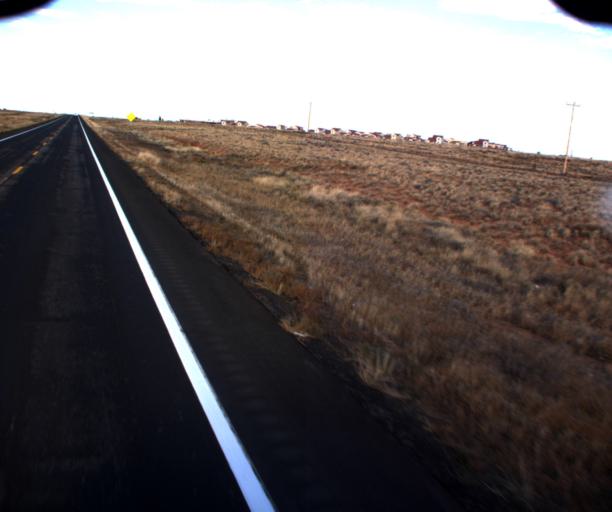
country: US
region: Arizona
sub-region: Apache County
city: Lukachukai
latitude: 36.9594
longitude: -109.3389
